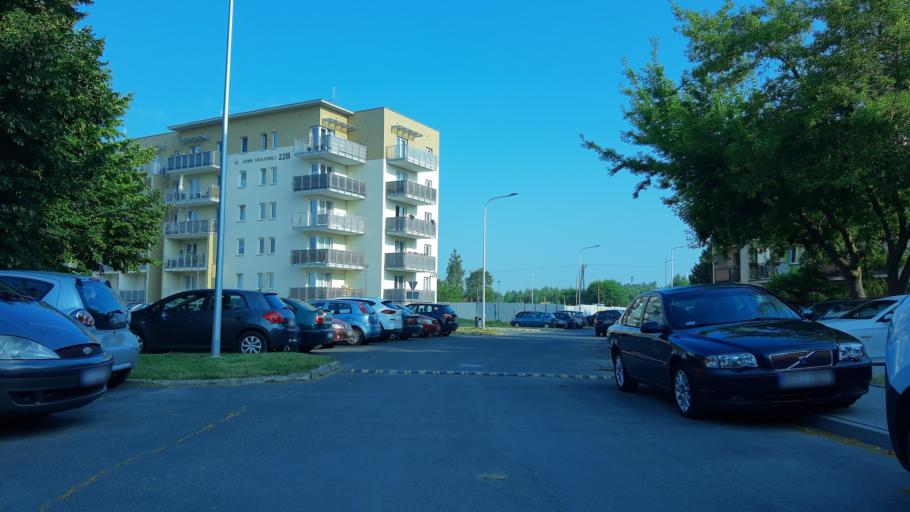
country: PL
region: Lodz Voivodeship
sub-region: Powiat sieradzki
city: Sieradz
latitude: 51.5843
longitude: 18.7087
